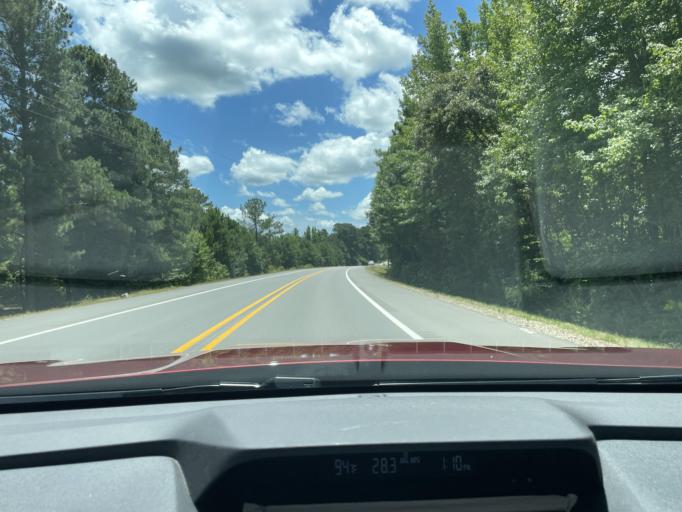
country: US
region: Arkansas
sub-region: Drew County
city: Monticello
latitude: 33.7212
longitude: -91.8103
